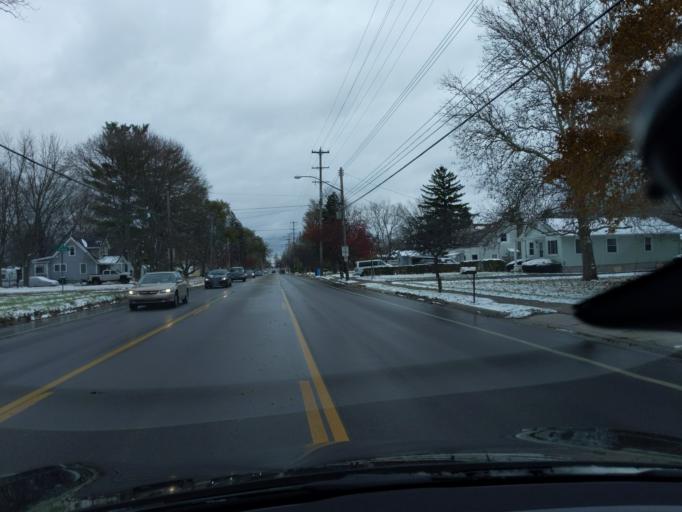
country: US
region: Michigan
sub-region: Ingham County
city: Lansing
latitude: 42.6831
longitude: -84.5867
